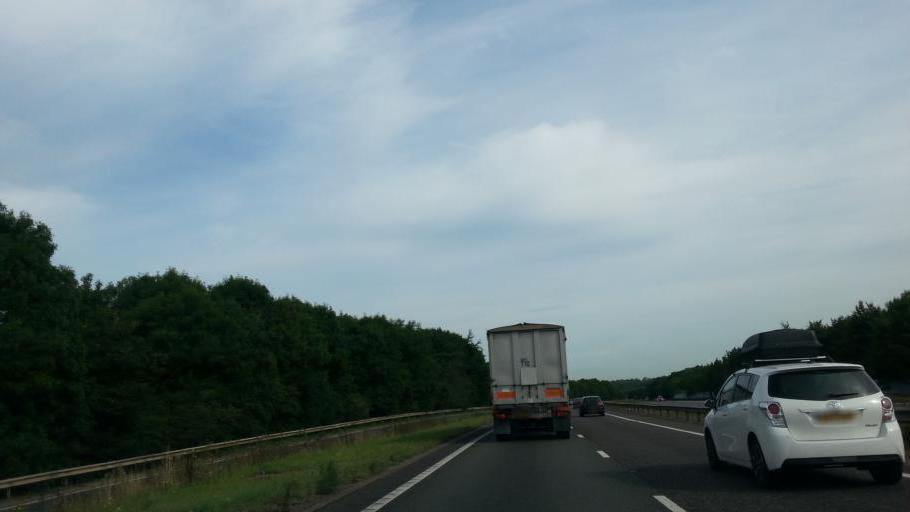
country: GB
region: England
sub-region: Suffolk
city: Bramford
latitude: 52.1055
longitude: 1.1064
